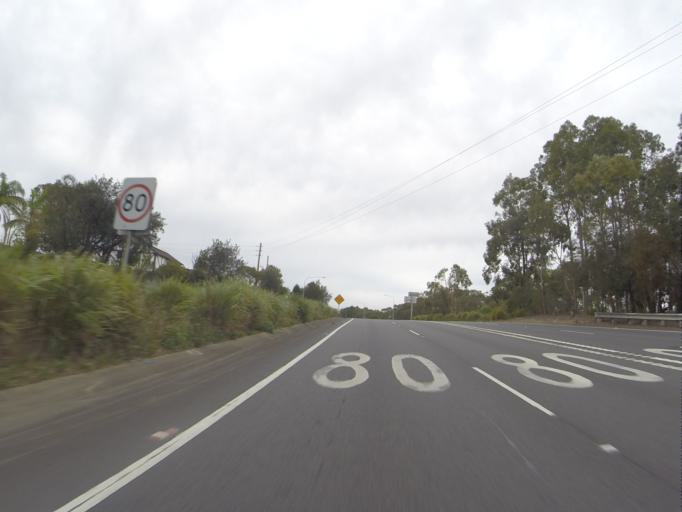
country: AU
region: New South Wales
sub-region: Hurstville
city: Lugarno
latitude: -33.9900
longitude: 151.0270
